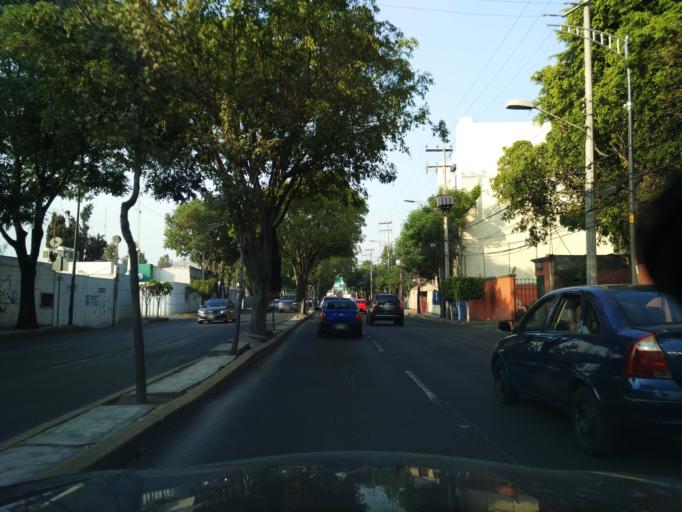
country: MX
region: Mexico City
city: Xochimilco
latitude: 19.2984
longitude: -99.1140
